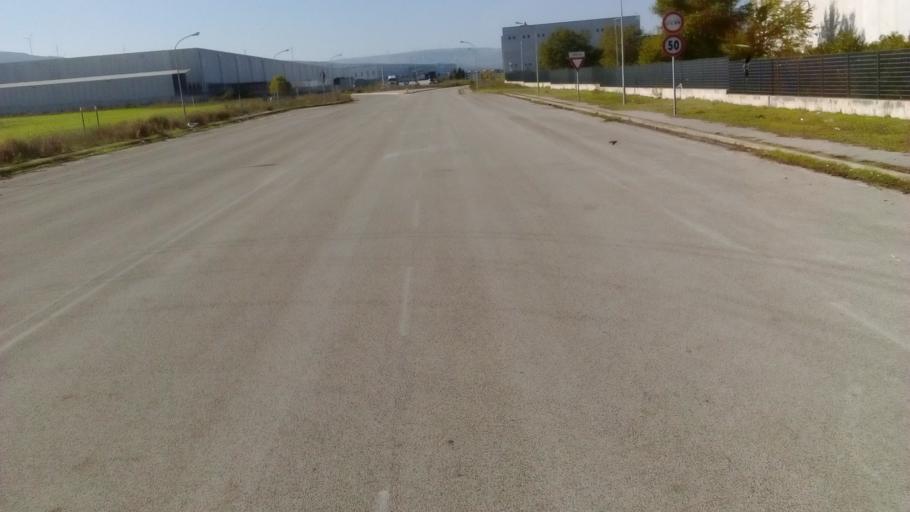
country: IT
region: Basilicate
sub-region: Provincia di Potenza
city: Melfi
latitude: 41.0782
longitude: 15.6618
